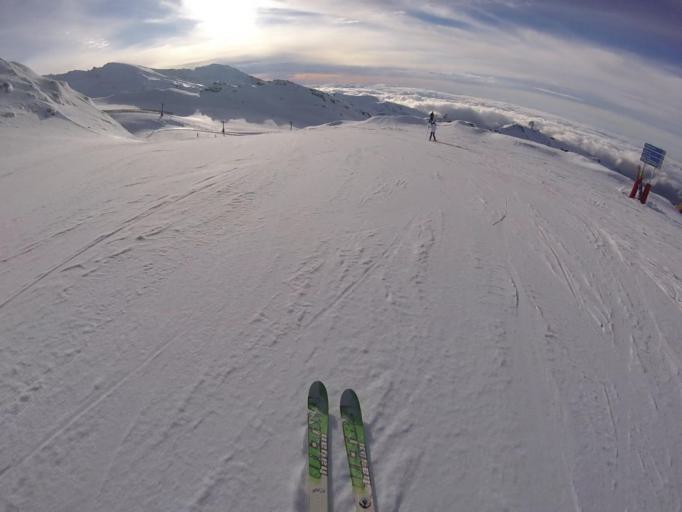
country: ES
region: Andalusia
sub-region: Provincia de Granada
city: Capileira
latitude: 37.0633
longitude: -3.3758
